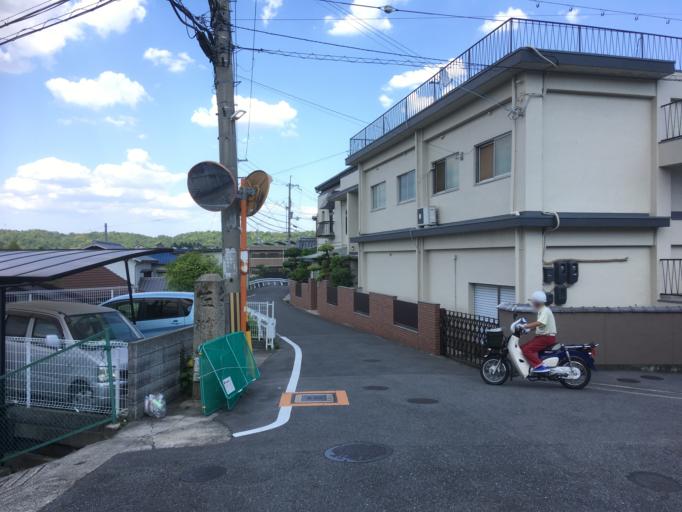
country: JP
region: Nara
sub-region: Ikoma-shi
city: Ikoma
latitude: 34.7013
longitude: 135.6939
